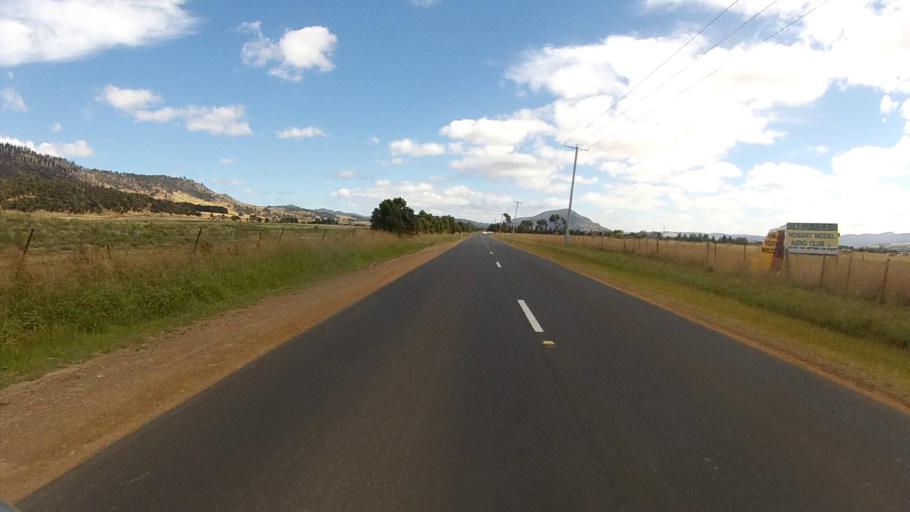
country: AU
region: Tasmania
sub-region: Clarence
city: Cambridge
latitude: -42.7193
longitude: 147.4333
